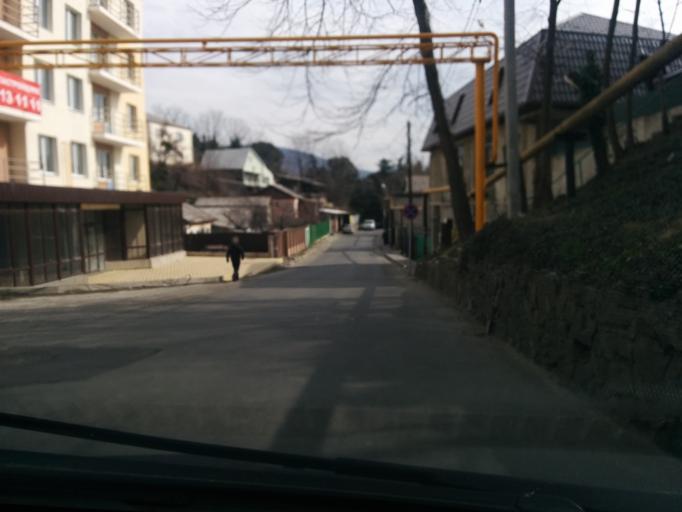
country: RU
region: Krasnodarskiy
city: Tuapse
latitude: 44.1019
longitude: 39.0763
